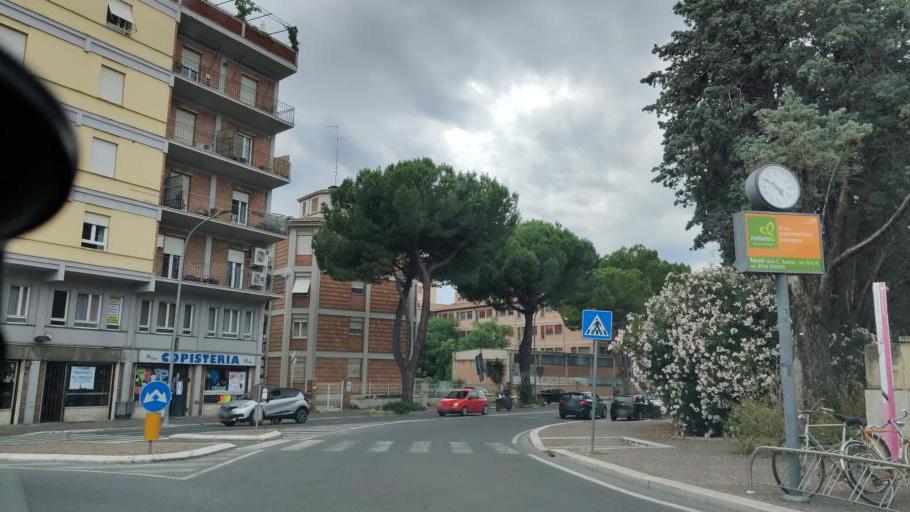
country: IT
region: Umbria
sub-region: Provincia di Terni
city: Terni
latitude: 42.5700
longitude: 12.6503
